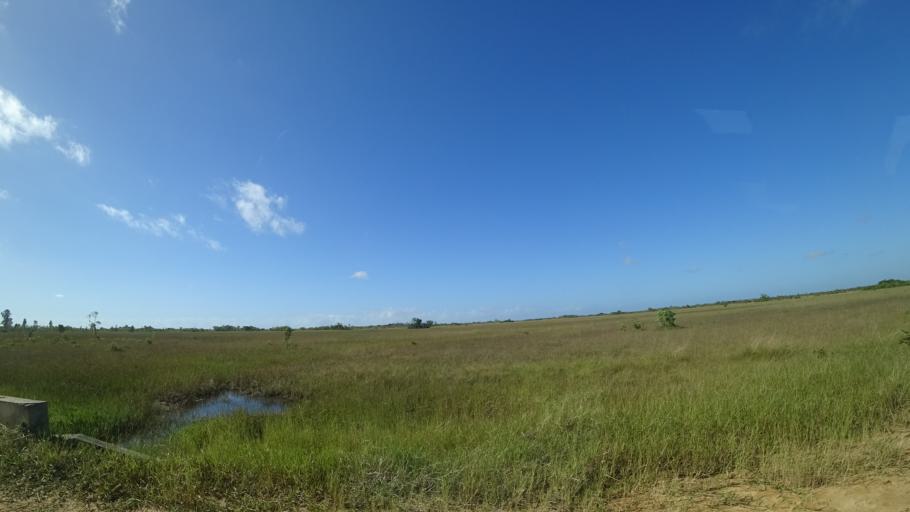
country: MZ
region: Sofala
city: Beira
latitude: -19.6935
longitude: 35.0374
